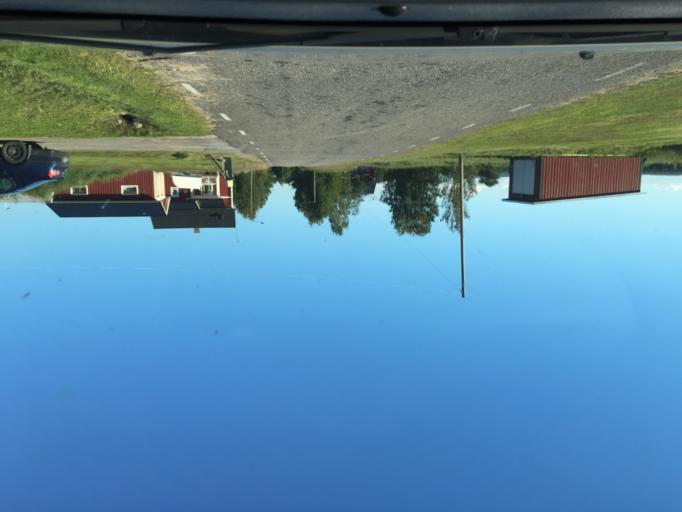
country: SE
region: Norrbotten
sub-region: Kalix Kommun
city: Toere
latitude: 66.1014
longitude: 22.7792
